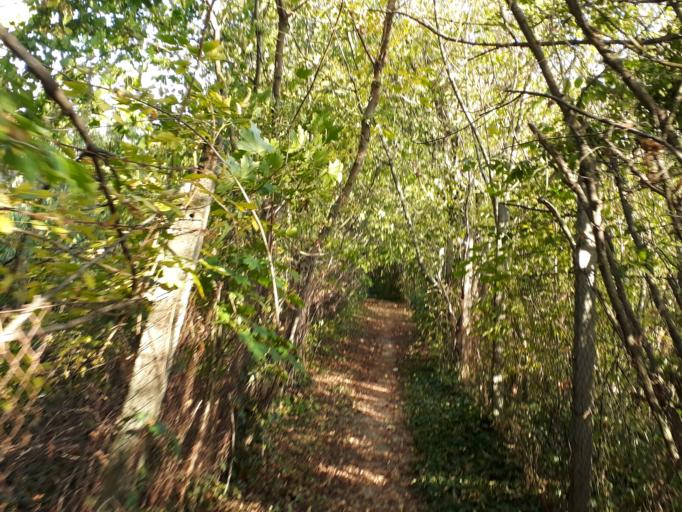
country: HU
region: Budapest
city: Budapest XII. keruelet
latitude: 47.4574
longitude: 18.9989
